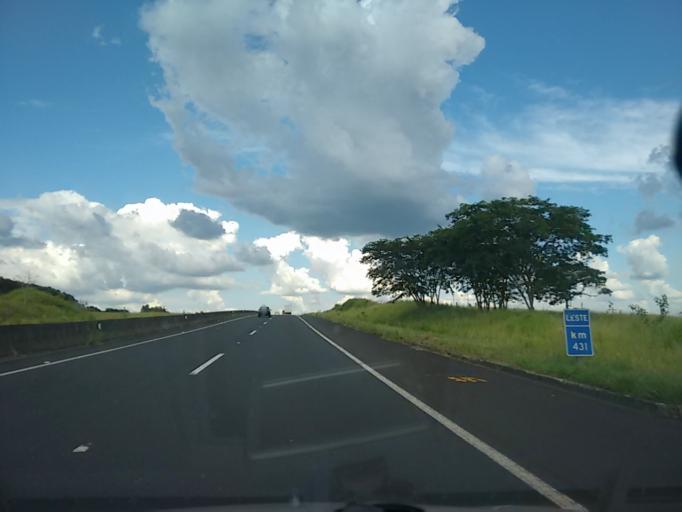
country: BR
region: Sao Paulo
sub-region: Garca
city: Garca
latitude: -22.2265
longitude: -49.7907
